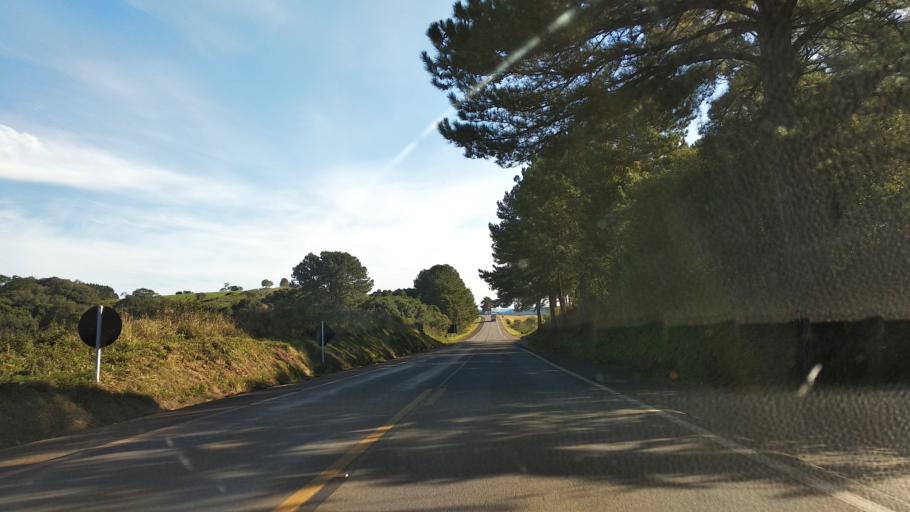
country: BR
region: Santa Catarina
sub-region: Celso Ramos
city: Celso Ramos
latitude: -27.5312
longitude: -51.3923
